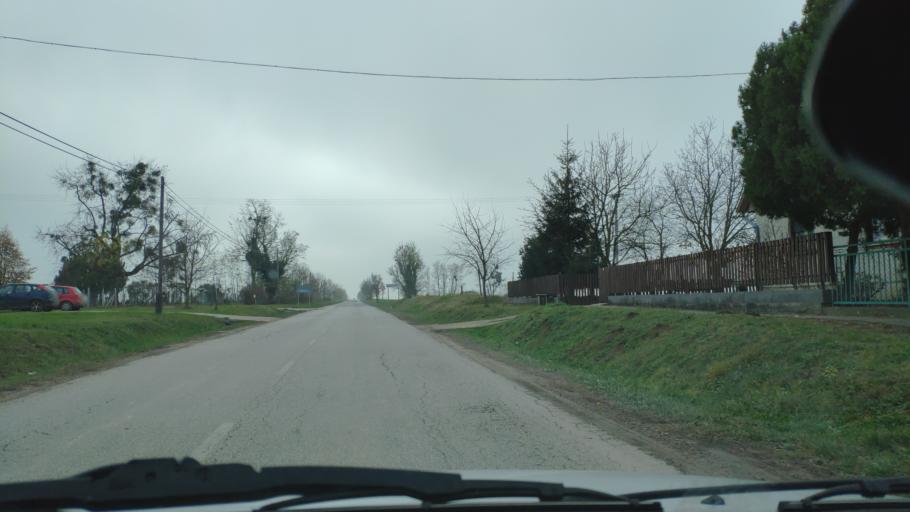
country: HU
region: Somogy
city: Balatonbereny
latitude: 46.6689
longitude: 17.2916
